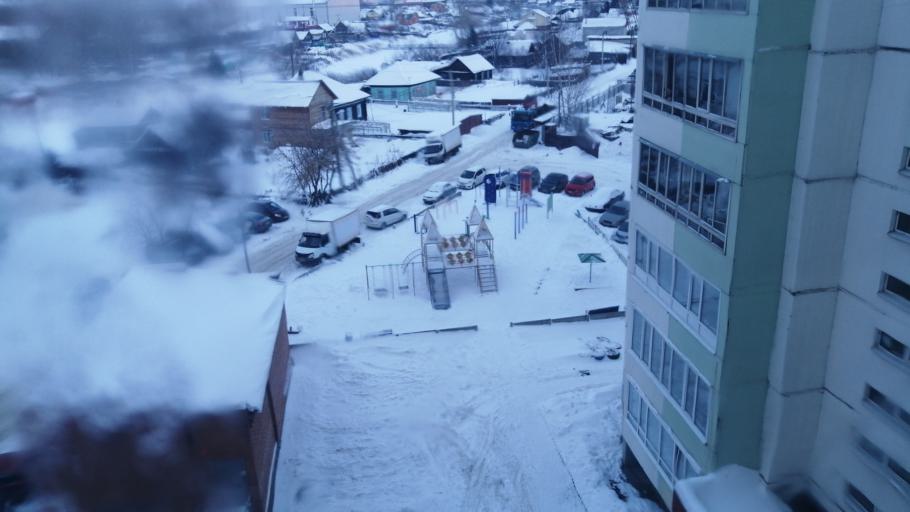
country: RU
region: Tomsk
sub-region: Tomskiy Rayon
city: Tomsk
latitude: 56.5223
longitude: 84.9373
